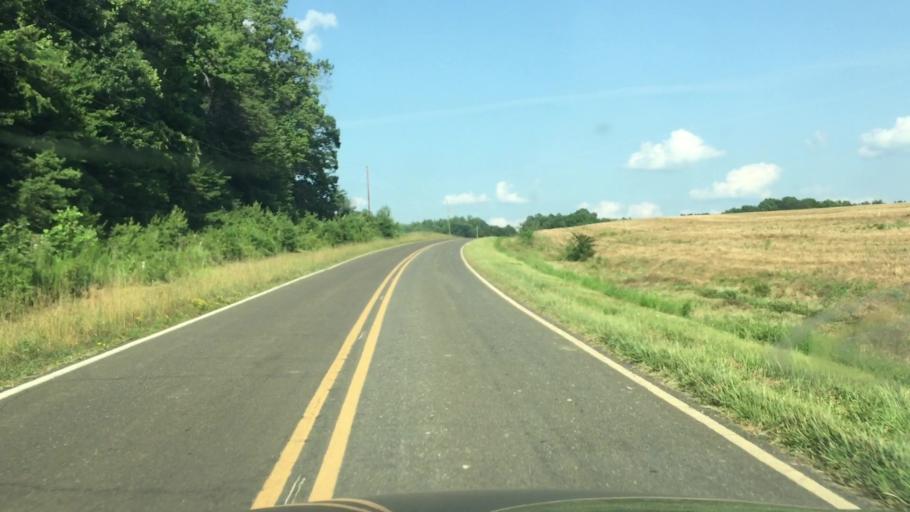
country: US
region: North Carolina
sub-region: Rockingham County
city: Reidsville
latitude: 36.2748
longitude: -79.5769
